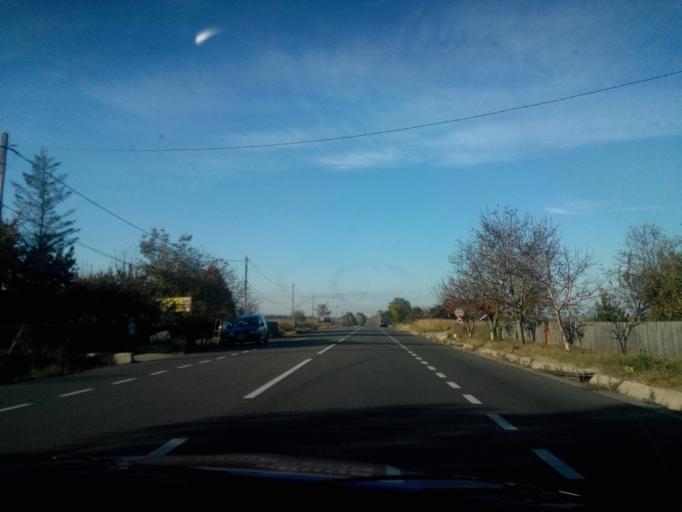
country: RO
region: Bacau
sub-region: Comuna Itesti
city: Itesti
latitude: 46.6781
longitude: 26.8990
